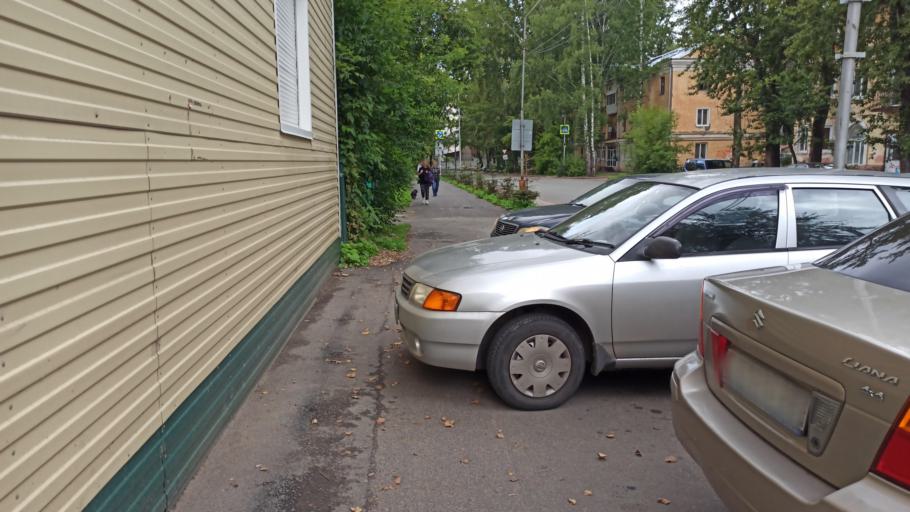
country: RU
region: Tomsk
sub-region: Tomskiy Rayon
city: Tomsk
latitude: 56.4625
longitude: 84.9831
